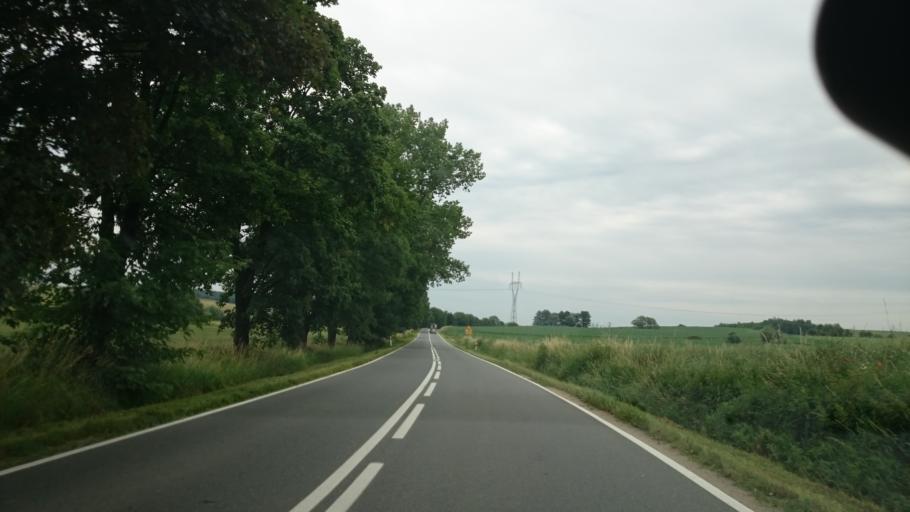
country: PL
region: Lower Silesian Voivodeship
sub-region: Powiat zabkowicki
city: Ziebice
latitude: 50.5872
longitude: 16.9655
